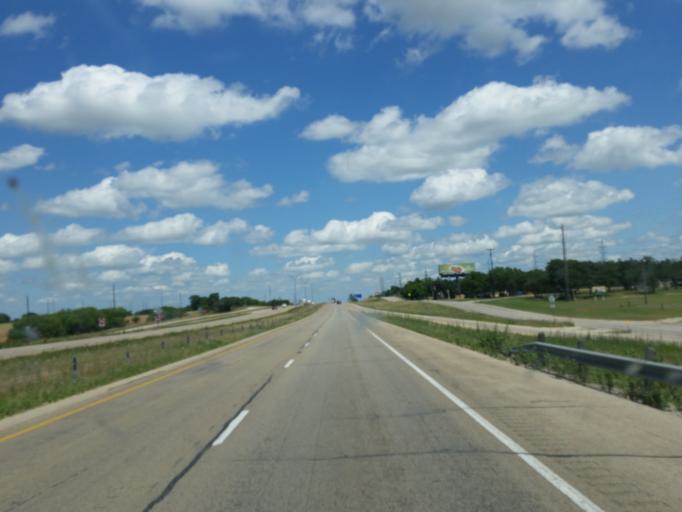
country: US
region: Texas
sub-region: Callahan County
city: Clyde
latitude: 32.4179
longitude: -99.5239
